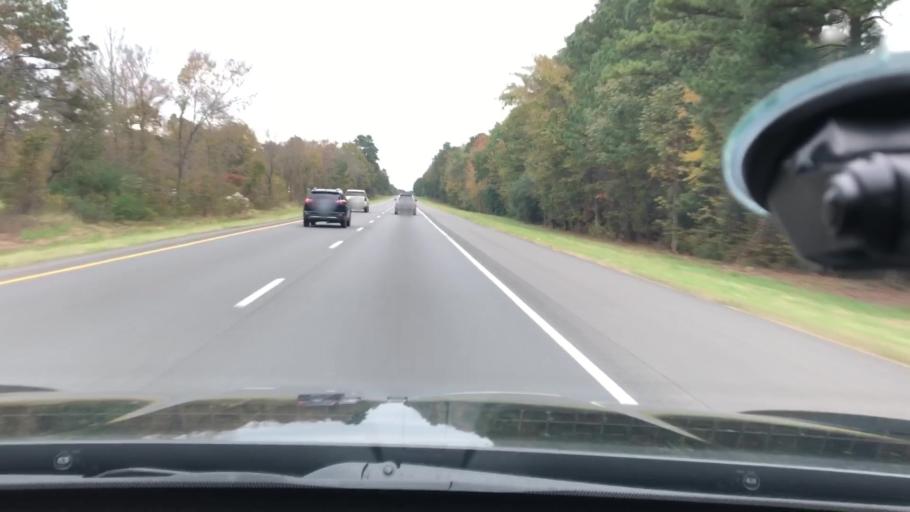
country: US
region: Arkansas
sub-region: Hempstead County
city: Hope
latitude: 33.7059
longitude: -93.5775
